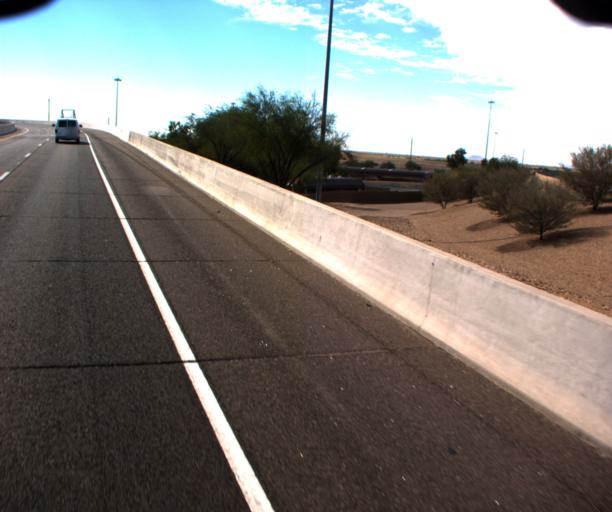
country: US
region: Arizona
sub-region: Maricopa County
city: Chandler
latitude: 33.2945
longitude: -111.8944
